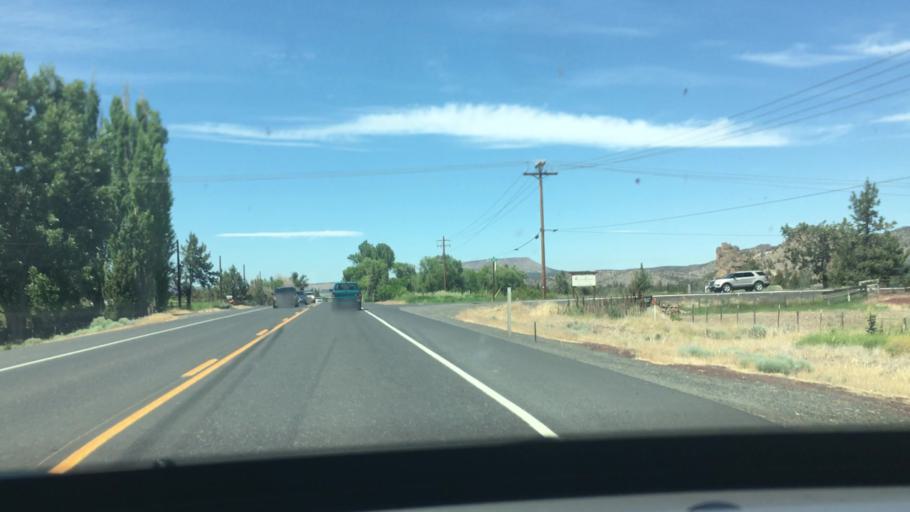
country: US
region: Oregon
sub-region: Deschutes County
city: Terrebonne
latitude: 44.3699
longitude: -121.1785
